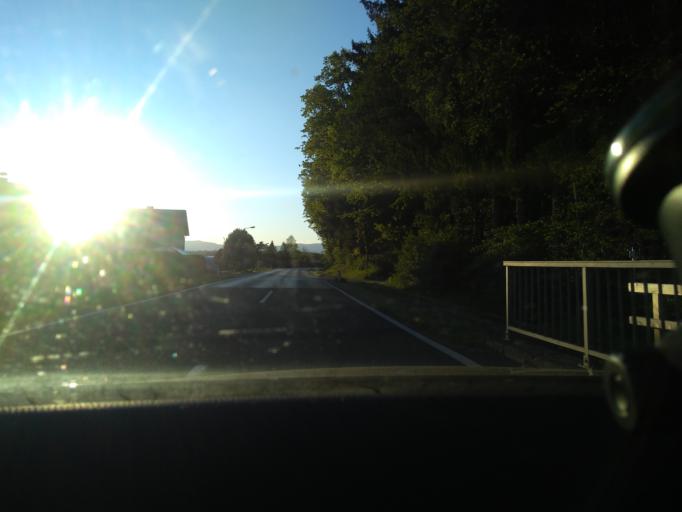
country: AT
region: Styria
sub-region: Politischer Bezirk Voitsberg
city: Mooskirchen
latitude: 46.9904
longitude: 15.3039
